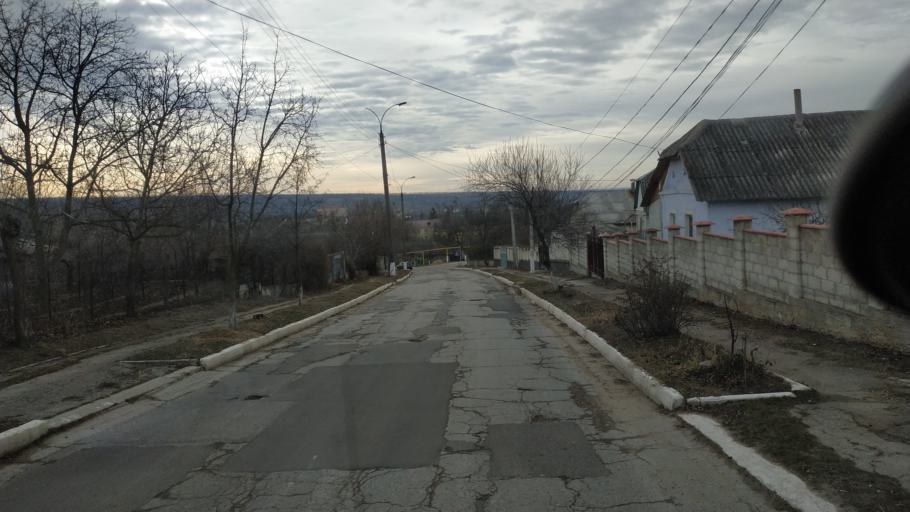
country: MD
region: Criuleni
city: Criuleni
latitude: 47.2171
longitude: 29.1587
